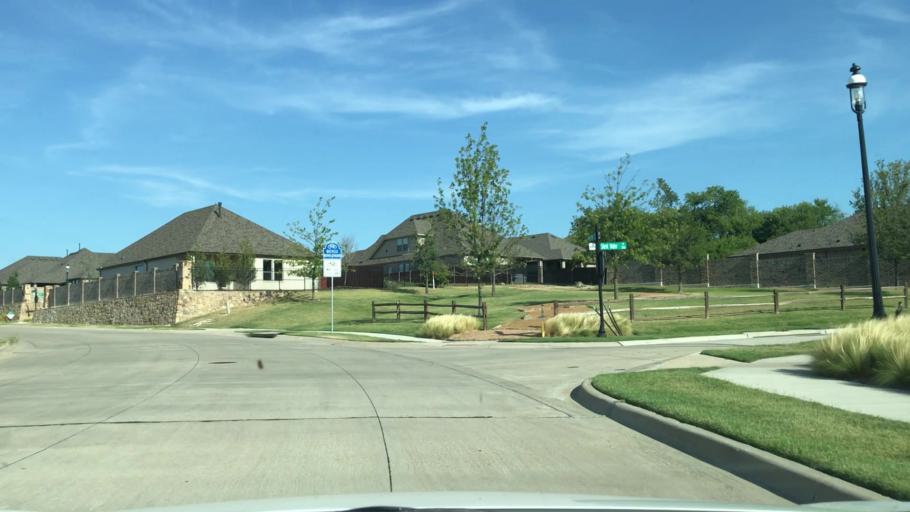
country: US
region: Texas
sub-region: Collin County
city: McKinney
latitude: 33.2400
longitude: -96.6501
